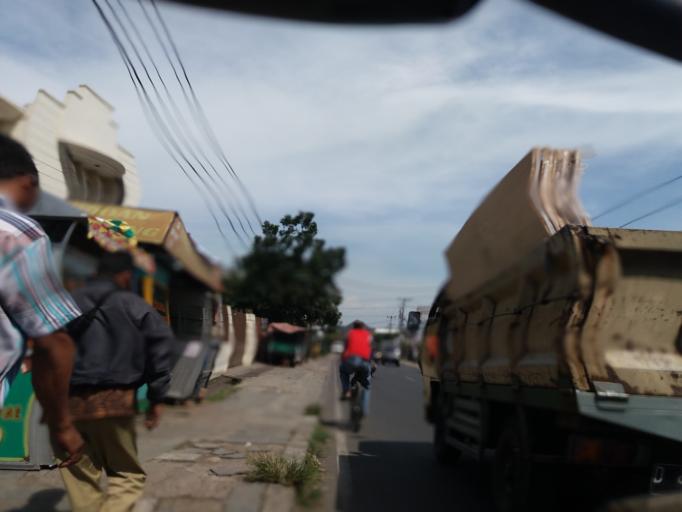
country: ID
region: West Java
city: Margahayukencana
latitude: -6.9343
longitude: 107.5715
